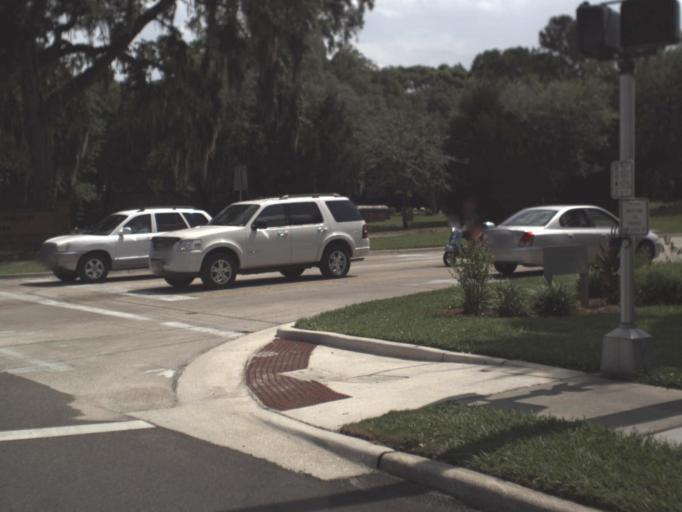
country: US
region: Florida
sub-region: Alachua County
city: Gainesville
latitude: 29.6789
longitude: -82.3390
